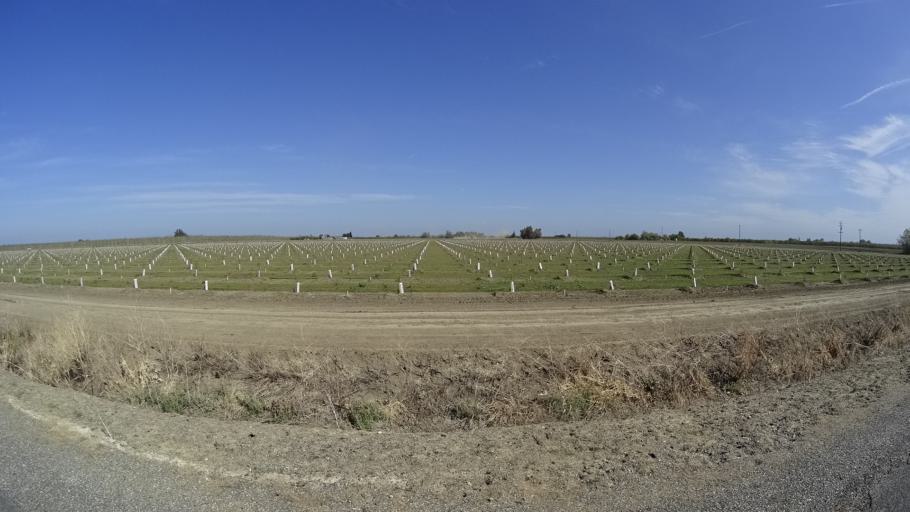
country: US
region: California
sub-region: Glenn County
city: Hamilton City
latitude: 39.6163
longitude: -122.0386
